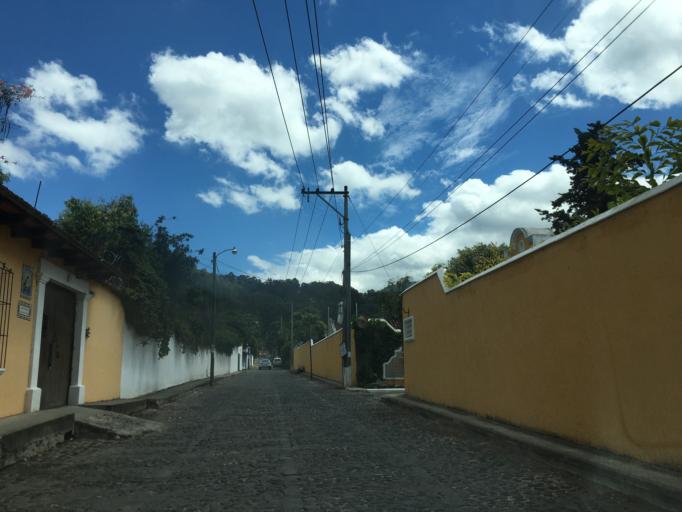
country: GT
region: Sacatepequez
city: Antigua Guatemala
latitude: 14.5621
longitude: -90.7265
